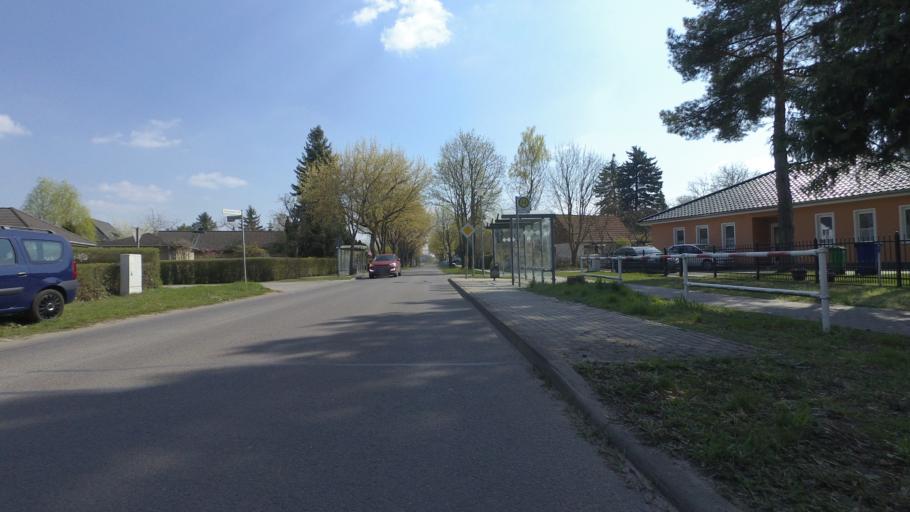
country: DE
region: Brandenburg
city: Rangsdorf
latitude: 52.2847
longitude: 13.4550
